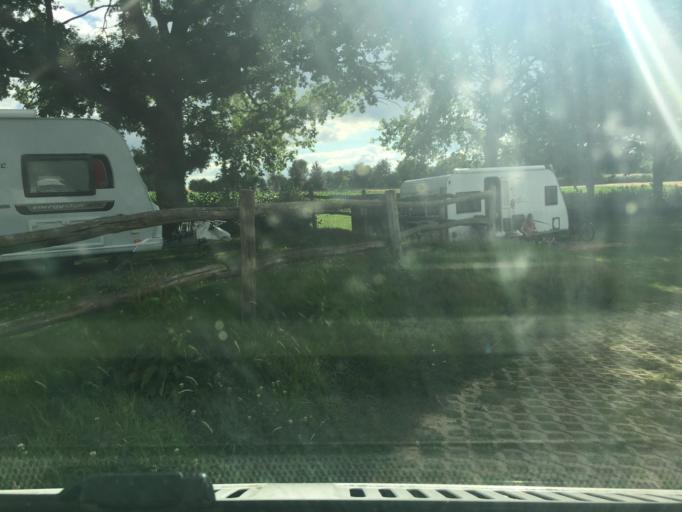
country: NL
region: Limburg
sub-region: Gemeente Vaals
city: Vaals
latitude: 50.7805
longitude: 6.0073
